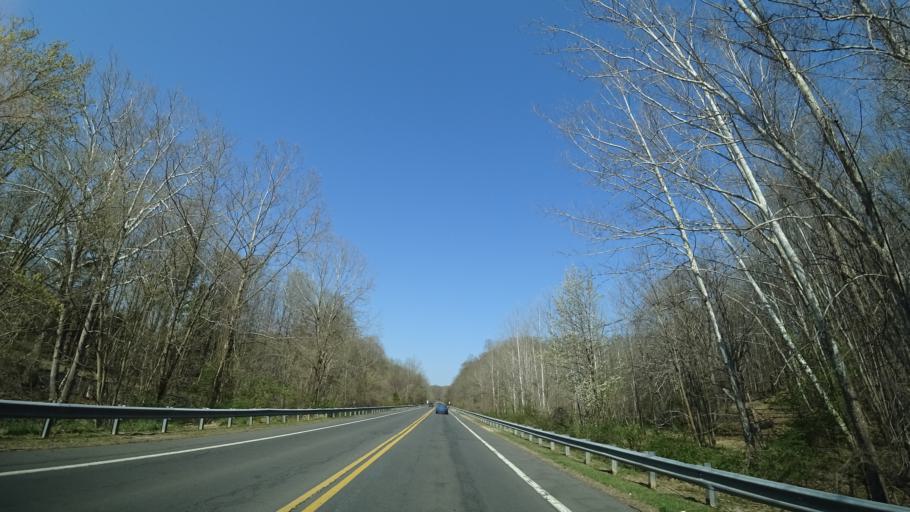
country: US
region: Maryland
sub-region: Montgomery County
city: Potomac
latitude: 39.0223
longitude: -77.1718
